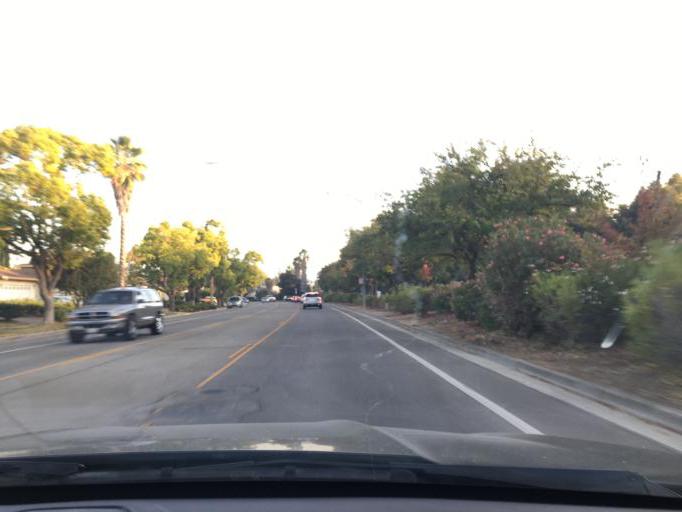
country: US
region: California
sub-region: Santa Clara County
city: Cupertino
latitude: 37.2954
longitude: -122.0407
